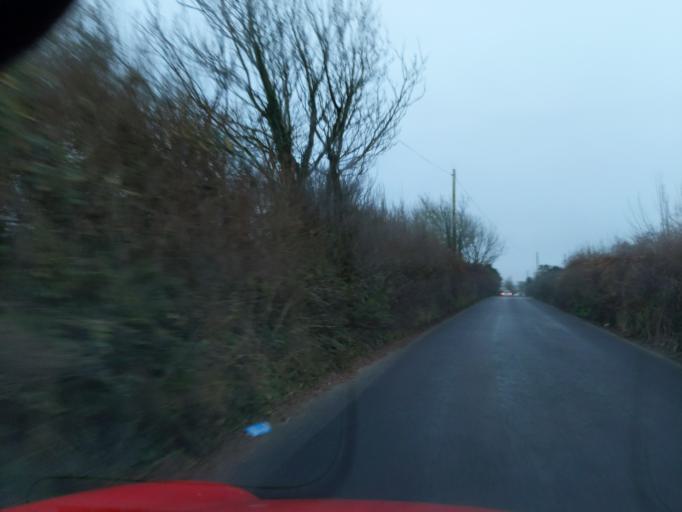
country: GB
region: England
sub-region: Devon
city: Wembury
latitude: 50.3309
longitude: -4.0638
